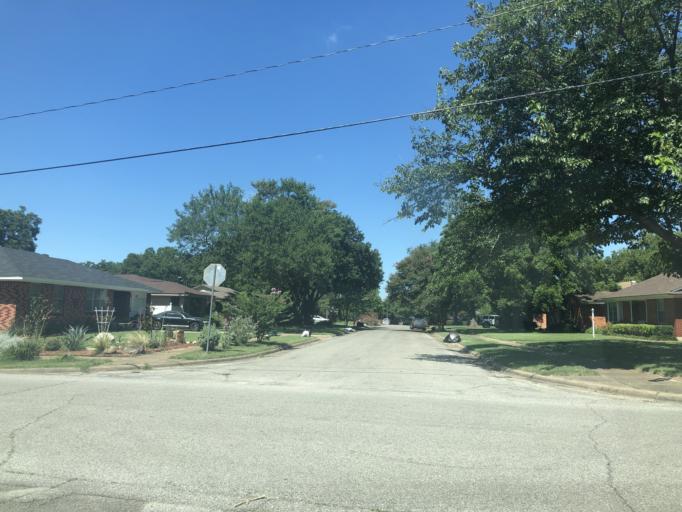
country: US
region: Texas
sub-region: Dallas County
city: Duncanville
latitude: 32.6536
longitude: -96.9131
